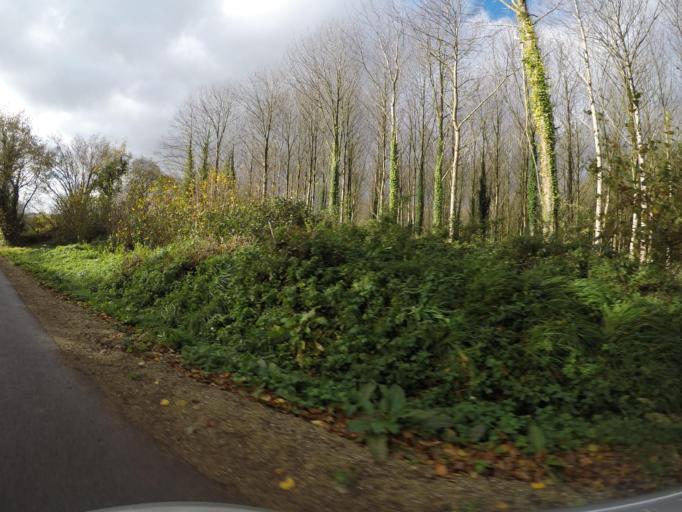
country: FR
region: Brittany
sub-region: Departement des Cotes-d'Armor
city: Bourbriac
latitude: 48.4927
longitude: -3.1886
